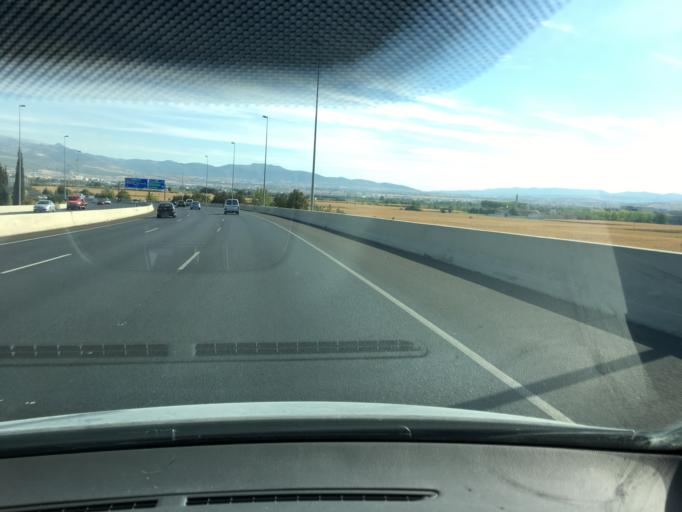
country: ES
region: Andalusia
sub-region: Provincia de Granada
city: Maracena
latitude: 37.1890
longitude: -3.6334
